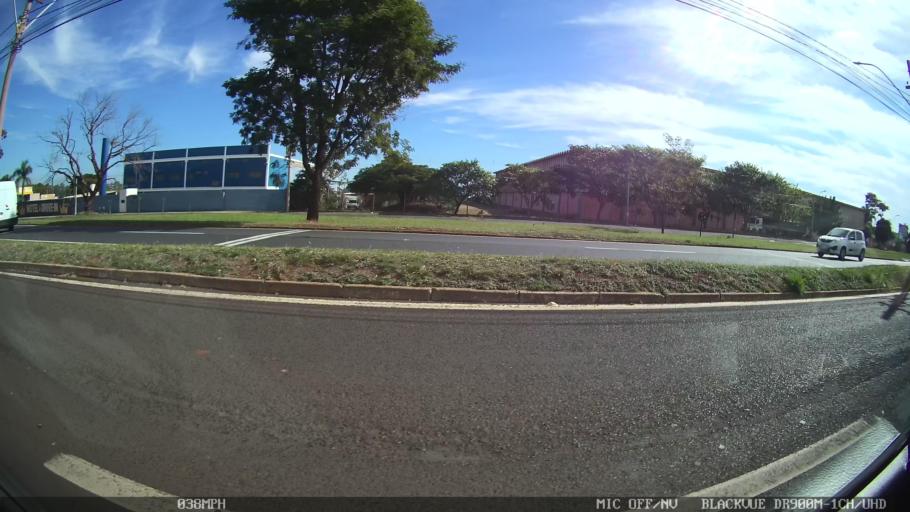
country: BR
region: Sao Paulo
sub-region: Araraquara
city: Araraquara
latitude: -21.8162
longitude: -48.1574
